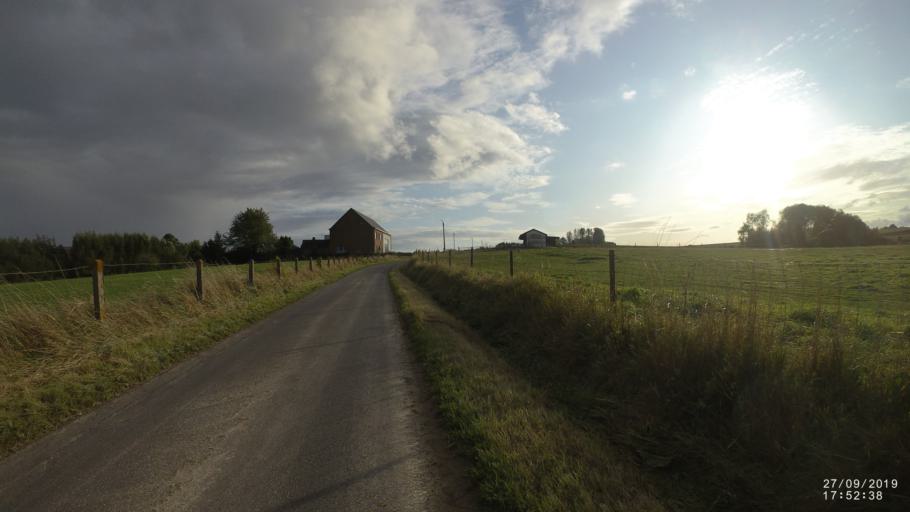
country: BE
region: Wallonia
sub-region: Province du Hainaut
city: Flobecq
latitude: 50.8172
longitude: 3.7129
